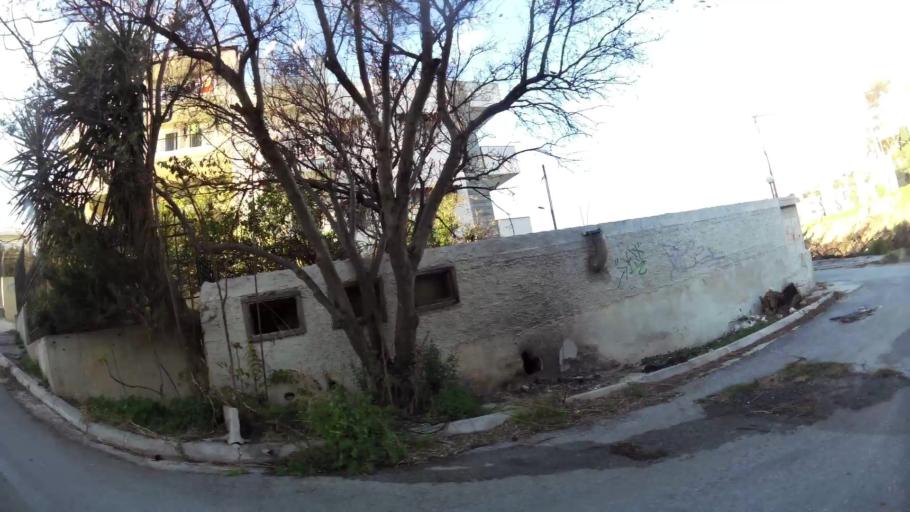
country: GR
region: Attica
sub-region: Nomarchia Anatolikis Attikis
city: Rafina
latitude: 38.0262
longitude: 24.0013
